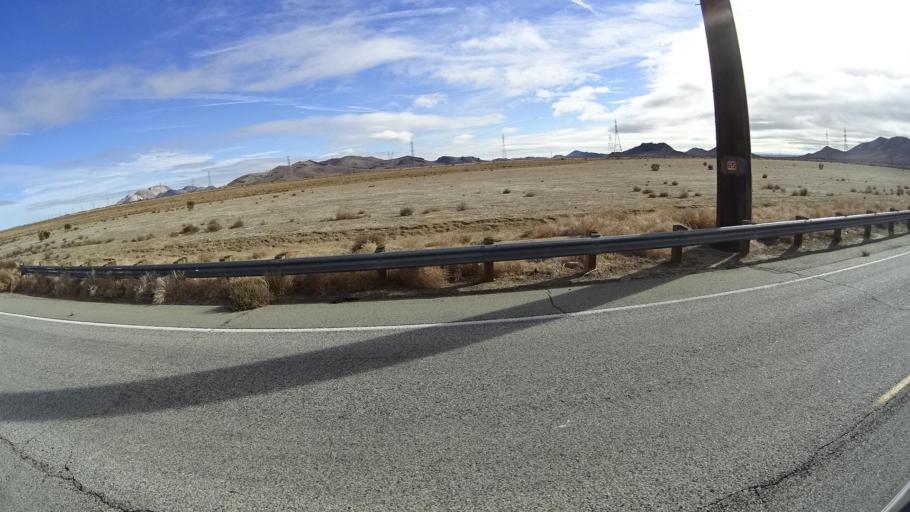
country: US
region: California
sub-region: Kern County
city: Rosamond
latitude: 34.9100
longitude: -118.2914
